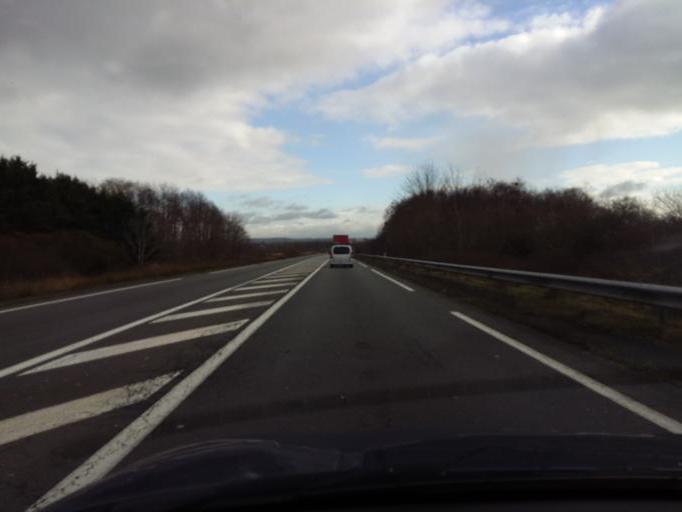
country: FR
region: Auvergne
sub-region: Departement de l'Allier
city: Dompierre-sur-Besbre
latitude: 46.5408
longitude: 3.6711
